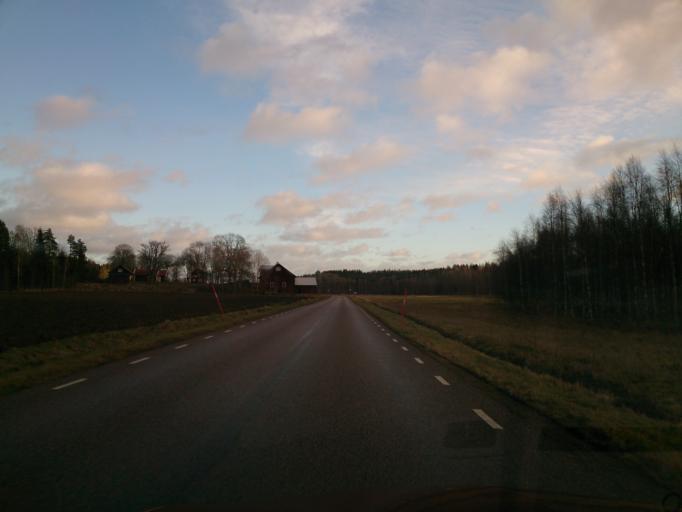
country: SE
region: OEstergoetland
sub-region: Atvidabergs Kommun
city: Atvidaberg
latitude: 58.2864
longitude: 16.0292
